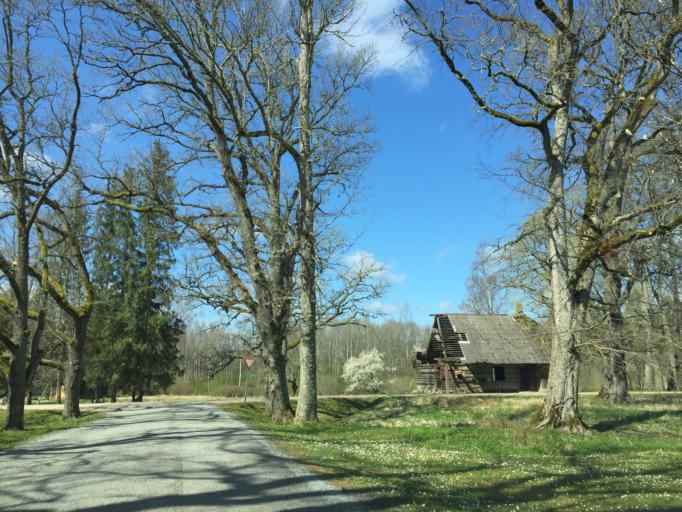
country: EE
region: Valgamaa
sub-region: Valga linn
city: Valga
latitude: 57.5927
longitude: 26.0420
